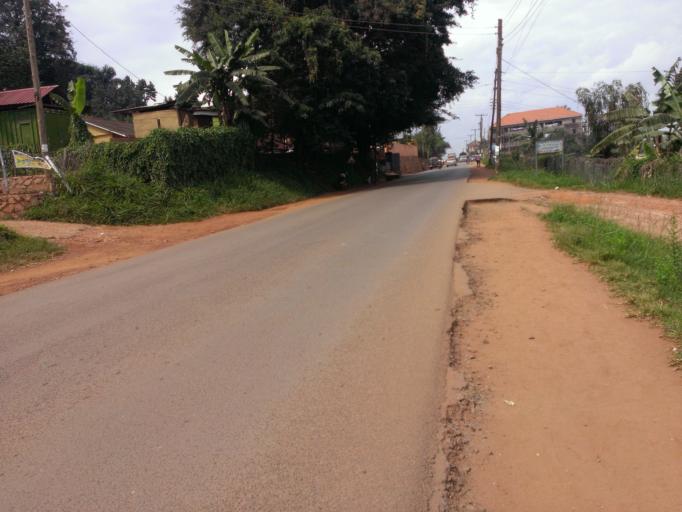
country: UG
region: Central Region
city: Kampala Central Division
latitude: 0.3160
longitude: 32.5575
